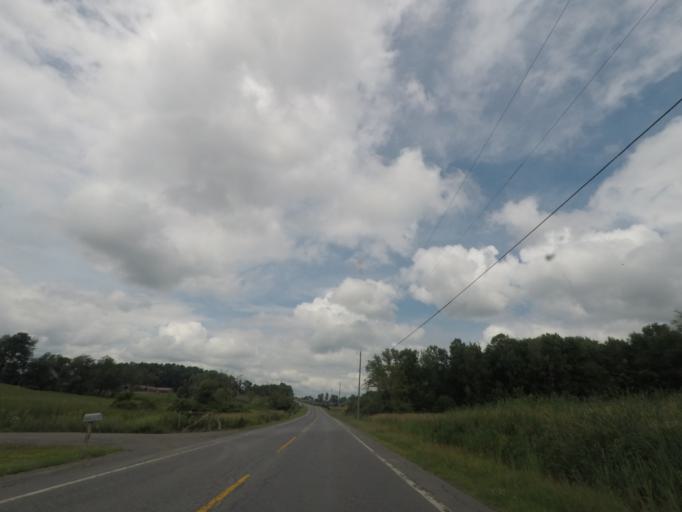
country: US
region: New York
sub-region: Saratoga County
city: Stillwater
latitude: 43.0263
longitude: -73.6880
